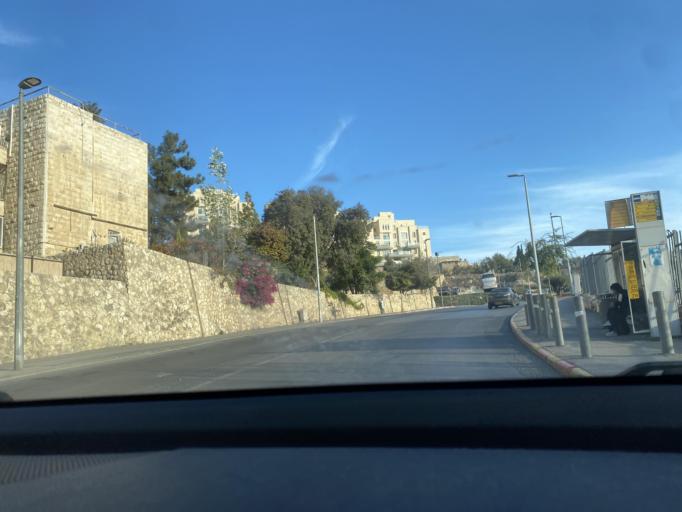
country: PS
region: West Bank
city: Ash Shaykh Sa`d
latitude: 31.7452
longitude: 35.2393
